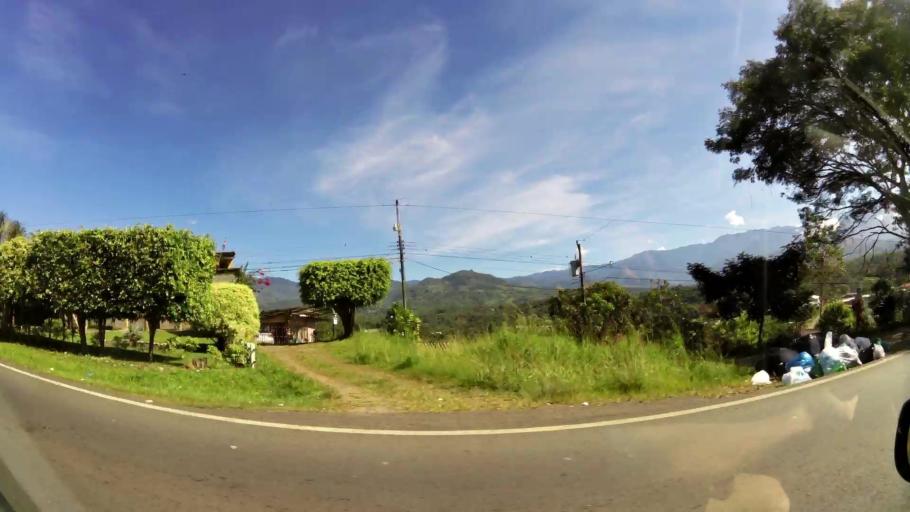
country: CR
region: San Jose
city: San Isidro
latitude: 9.3916
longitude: -83.7079
